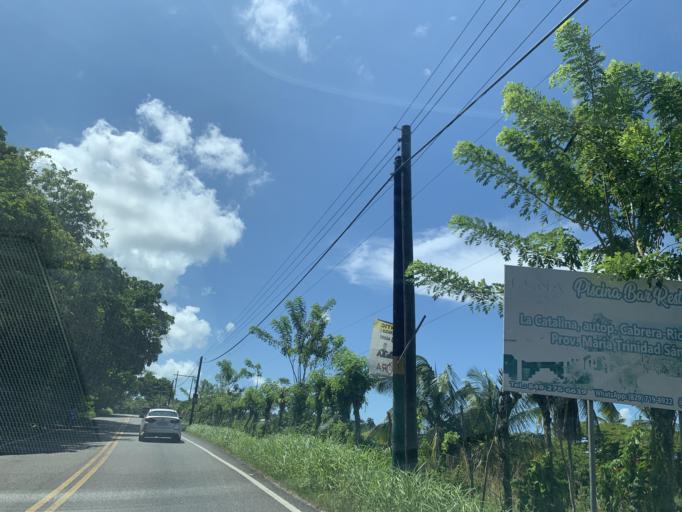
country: DO
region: Maria Trinidad Sanchez
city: Cabrera
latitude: 19.6481
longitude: -69.9235
